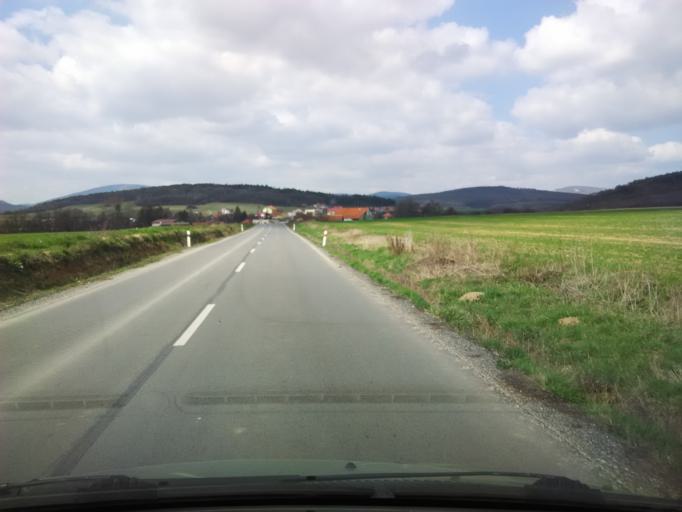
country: SK
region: Nitriansky
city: Zlate Moravce
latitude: 48.4242
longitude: 18.3314
